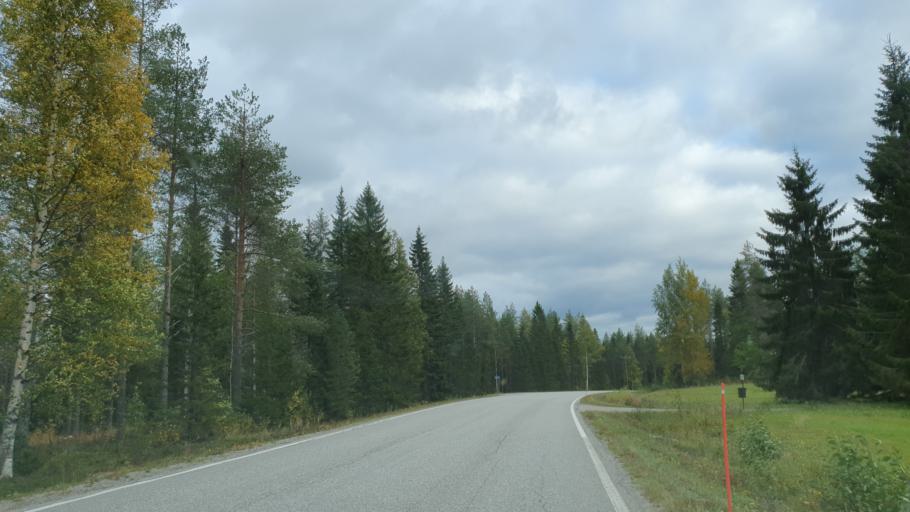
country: FI
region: Kainuu
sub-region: Kehys-Kainuu
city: Kuhmo
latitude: 63.9621
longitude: 29.6930
